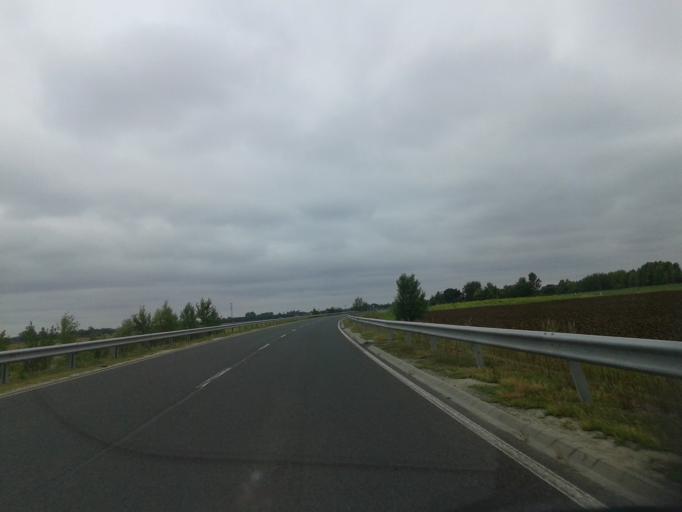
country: HU
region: Bacs-Kiskun
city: Harta
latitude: 46.7182
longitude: 19.0221
